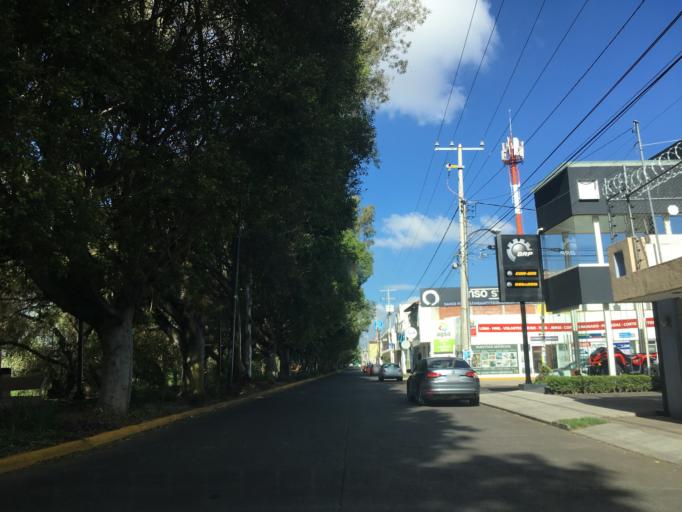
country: MX
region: Michoacan
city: Morelia
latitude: 19.6871
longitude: -101.1760
